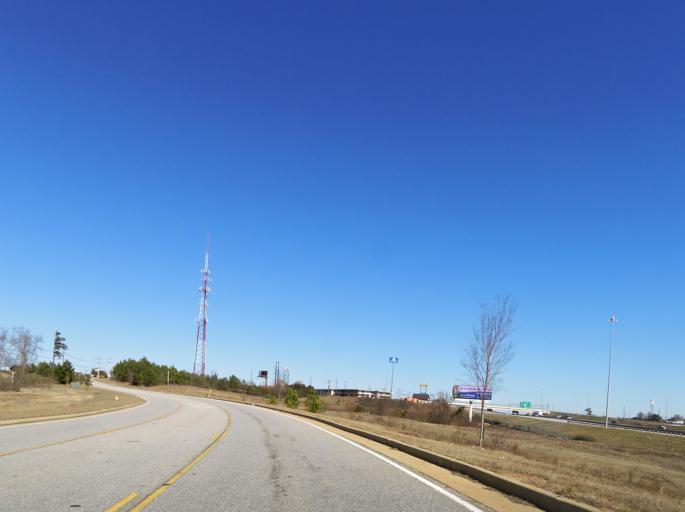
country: US
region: Georgia
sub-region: Peach County
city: Byron
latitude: 32.7404
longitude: -83.7227
